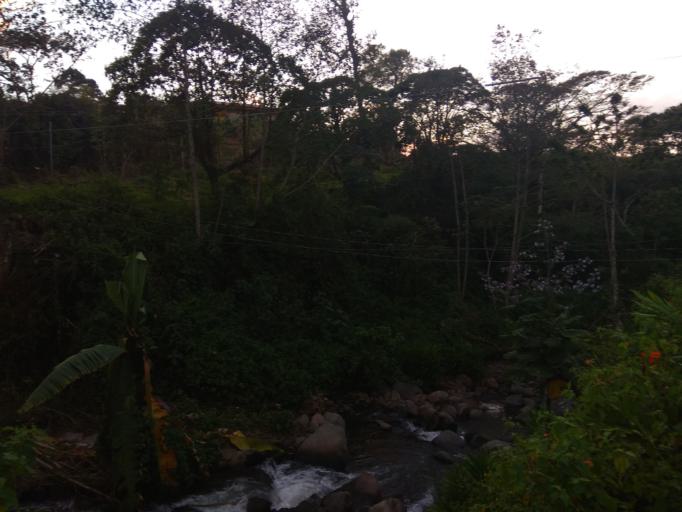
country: CR
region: San Jose
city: Ipis
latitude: 9.9802
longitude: -83.9727
